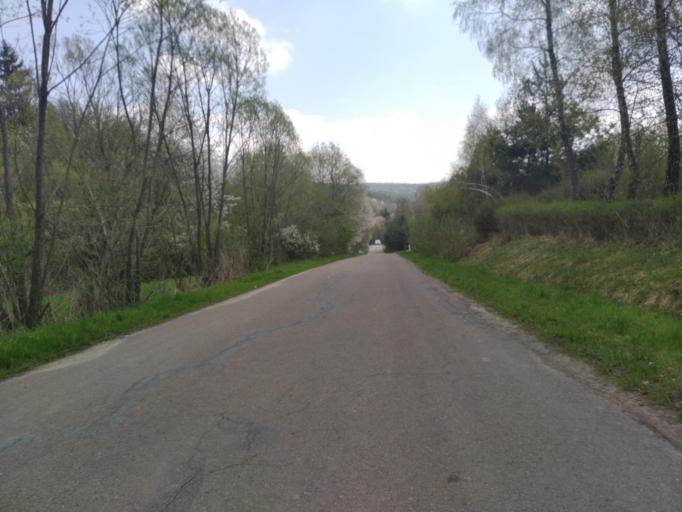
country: PL
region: Subcarpathian Voivodeship
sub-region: Powiat krosnienski
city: Iwonicz-Zdroj
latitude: 49.5247
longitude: 21.8183
